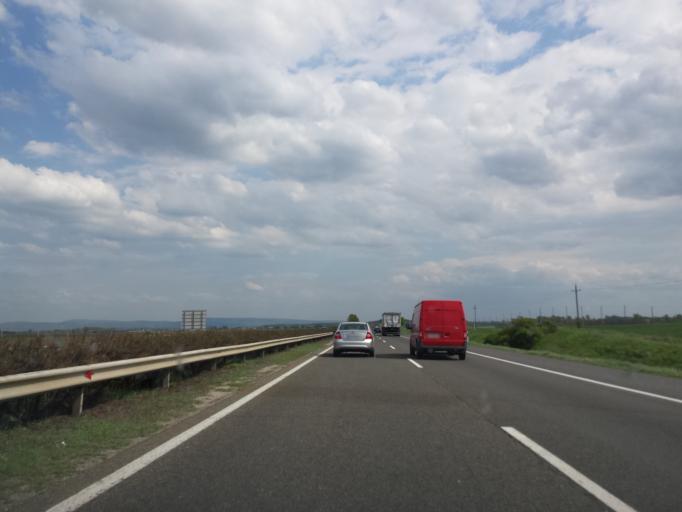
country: HU
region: Komarom-Esztergom
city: Nagyigmand
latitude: 47.6707
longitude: 18.1264
